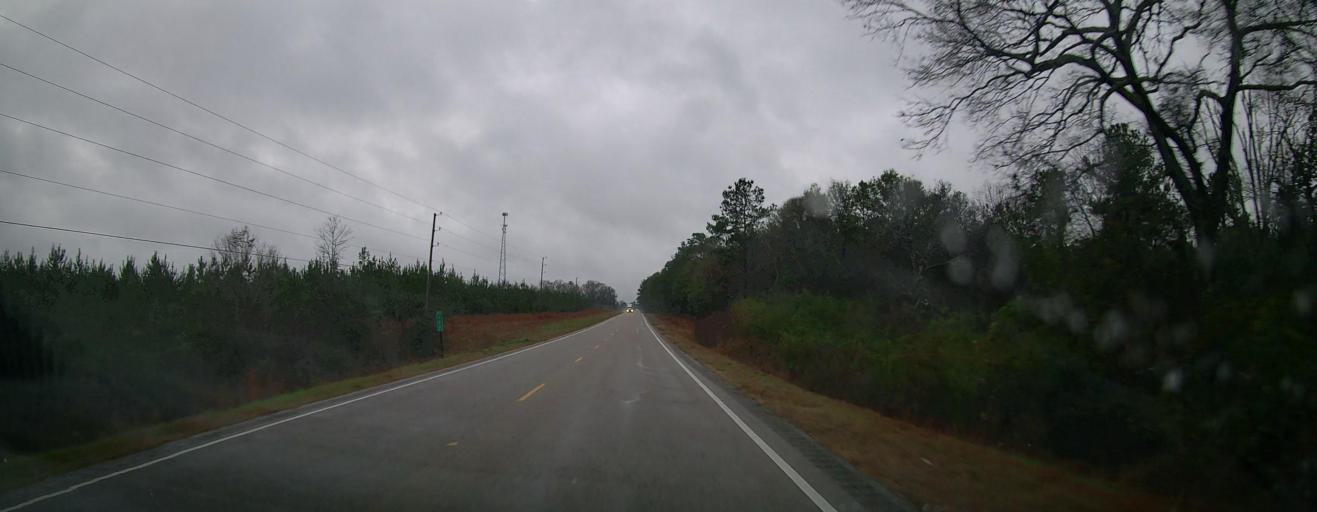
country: US
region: Alabama
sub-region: Autauga County
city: Pine Level
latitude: 32.5410
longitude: -86.6434
